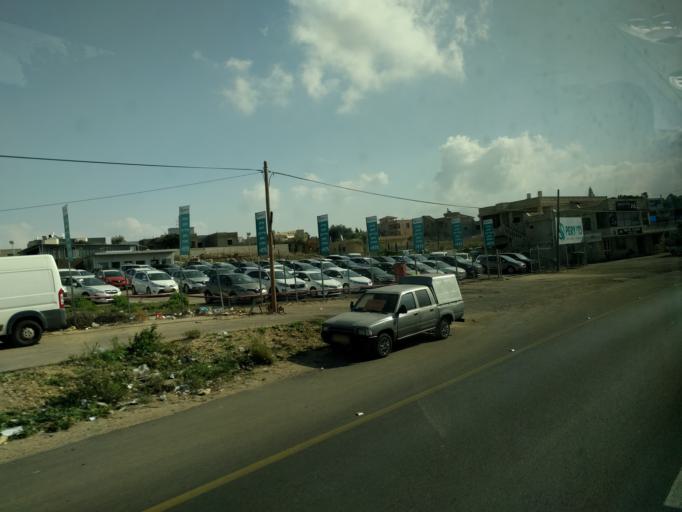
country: IL
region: Haifa
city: Daliyat el Karmil
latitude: 32.7079
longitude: 35.0672
